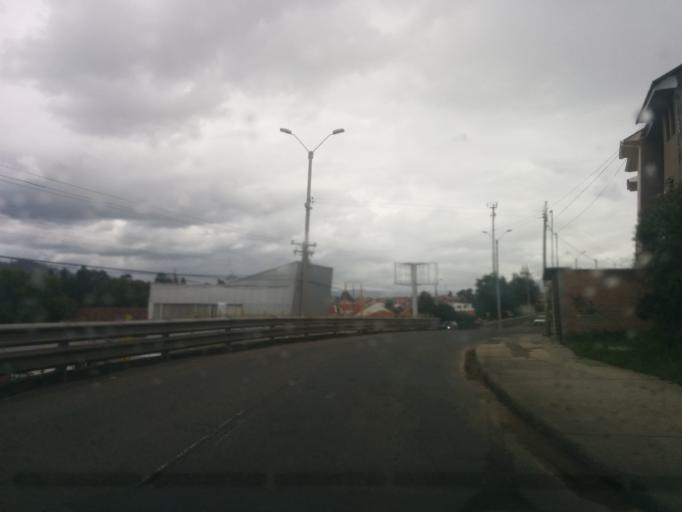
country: EC
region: Azuay
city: Cuenca
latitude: -2.8898
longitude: -78.9624
